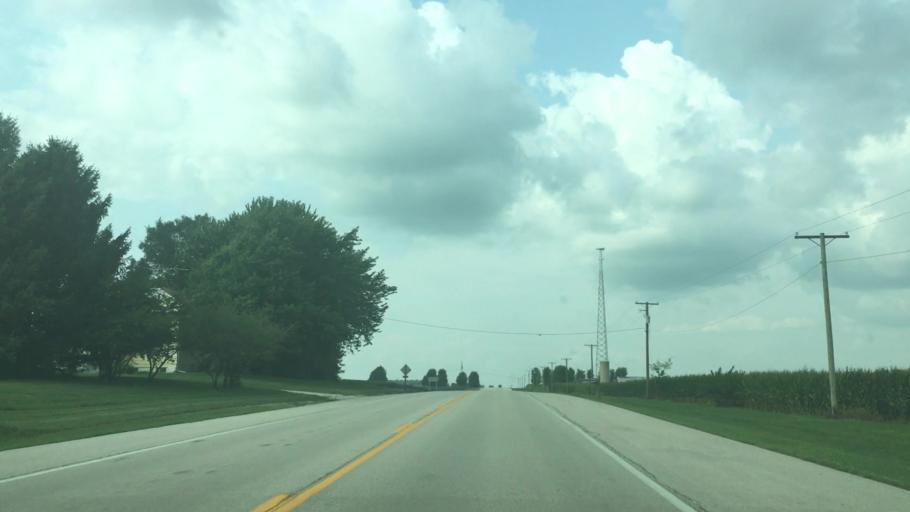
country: US
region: Illinois
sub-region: DeKalb County
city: Waterman
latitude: 41.7915
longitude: -88.7541
